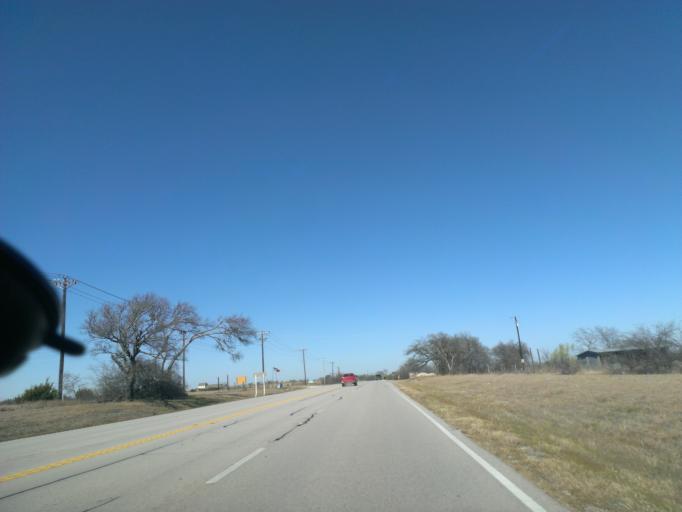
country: US
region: Texas
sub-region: Williamson County
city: Florence
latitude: 30.8428
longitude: -97.9047
